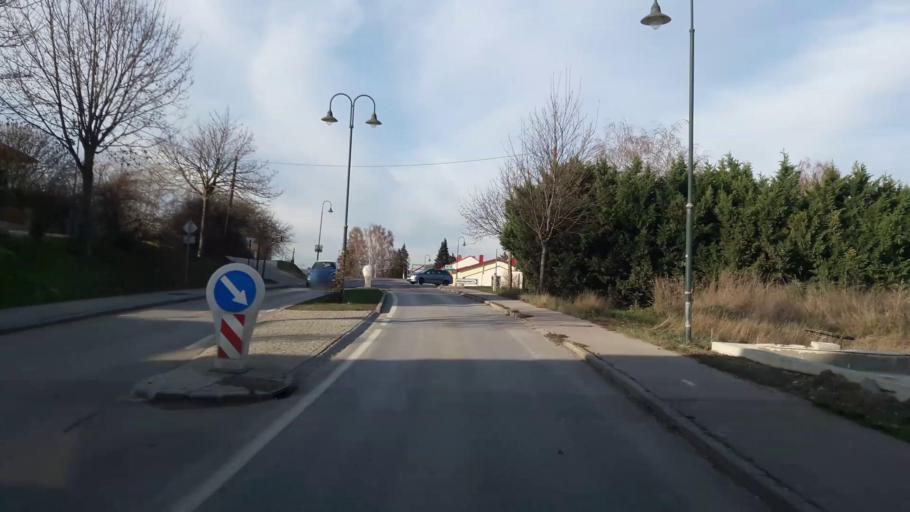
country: AT
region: Lower Austria
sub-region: Politischer Bezirk Ganserndorf
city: Gross-Schweinbarth
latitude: 48.4200
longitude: 16.6304
